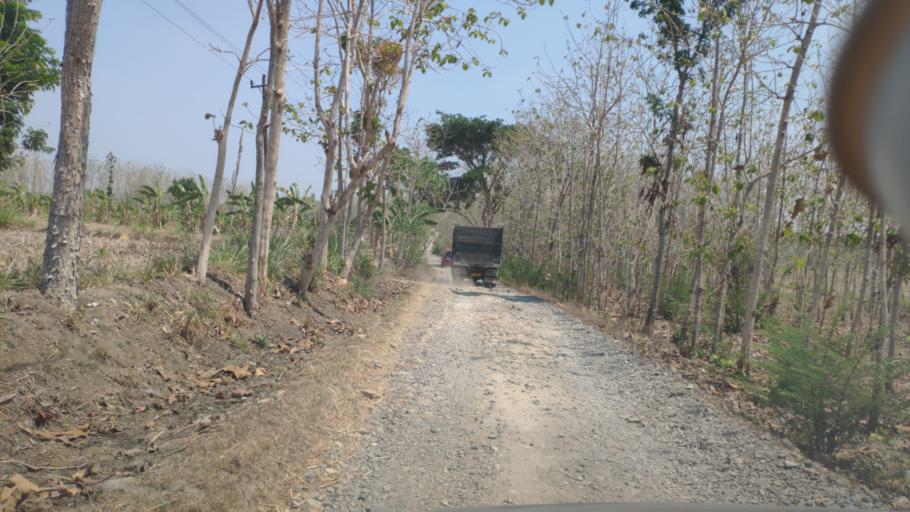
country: ID
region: Central Java
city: Balongrejo
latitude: -7.0070
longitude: 111.3657
